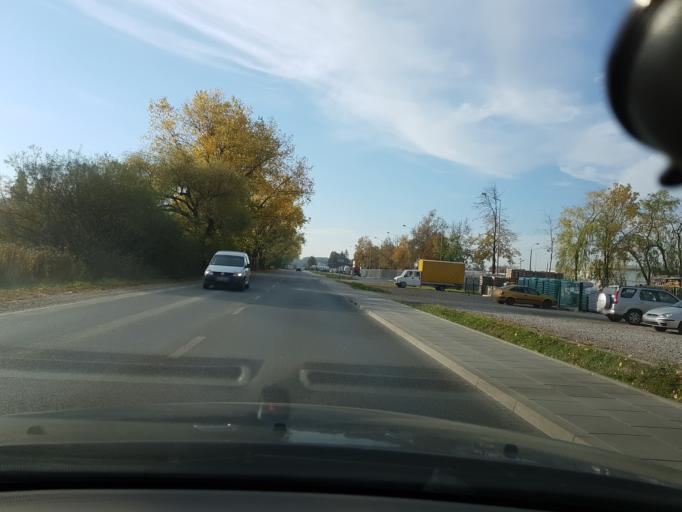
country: PL
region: Masovian Voivodeship
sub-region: Powiat warszawski zachodni
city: Babice
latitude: 52.2840
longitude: 20.8762
